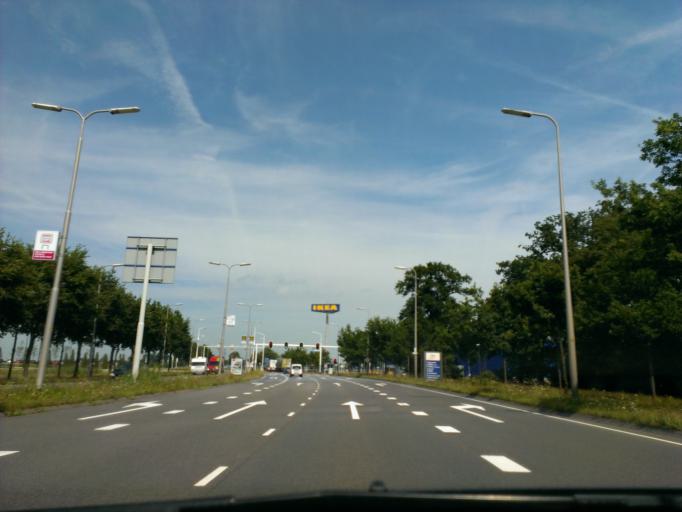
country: NL
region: Overijssel
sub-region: Gemeente Zwolle
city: Zwolle
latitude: 52.5313
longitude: 6.1586
